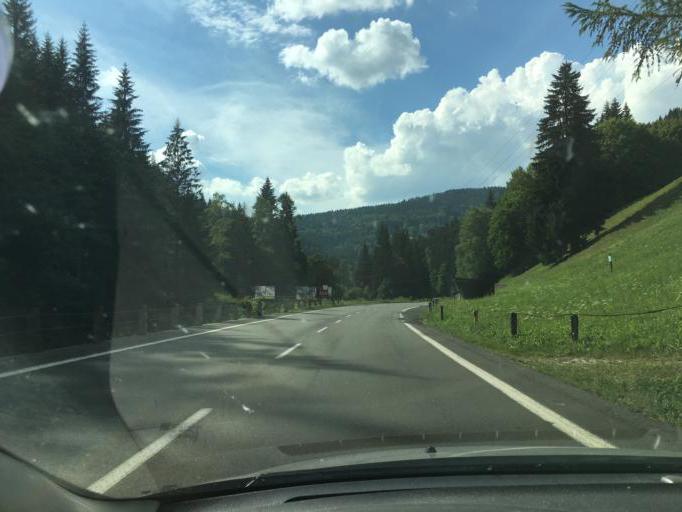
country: CZ
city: Benecko
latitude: 50.6807
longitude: 15.5900
